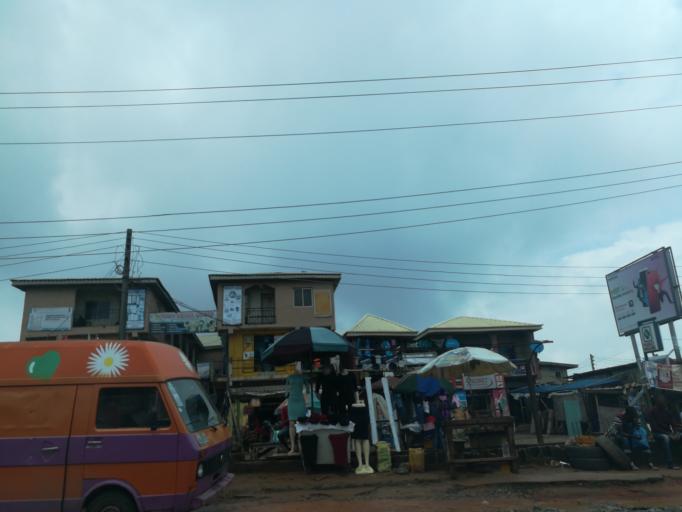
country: NG
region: Lagos
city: Ikorodu
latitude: 6.6619
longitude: 3.5195
